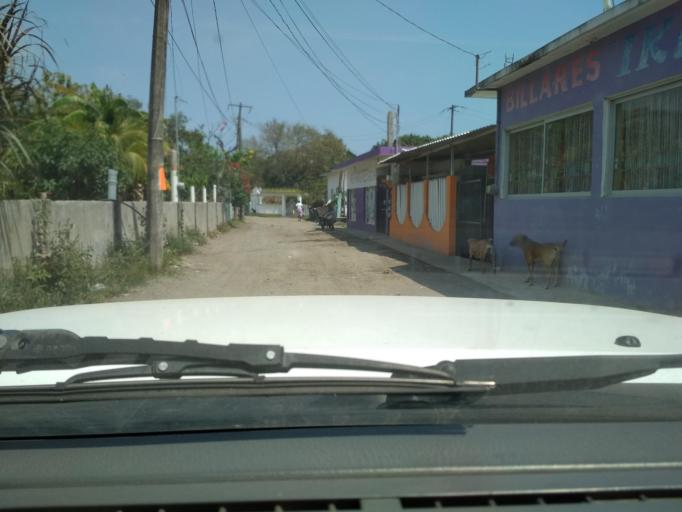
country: MX
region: Veracruz
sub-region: Medellin
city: Fraccionamiento Arboledas San Ramon
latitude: 19.0948
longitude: -96.1435
